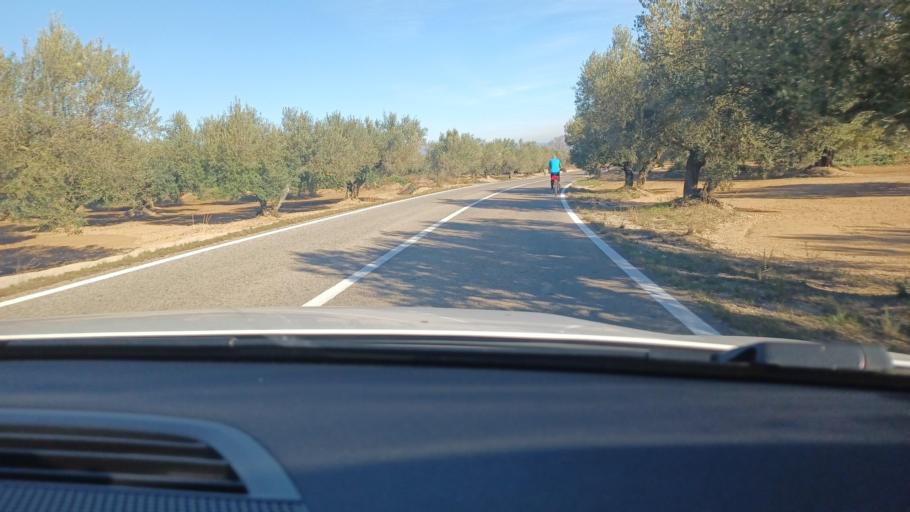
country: ES
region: Catalonia
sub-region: Provincia de Tarragona
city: Mas de Barberans
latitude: 40.7151
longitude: 0.4162
